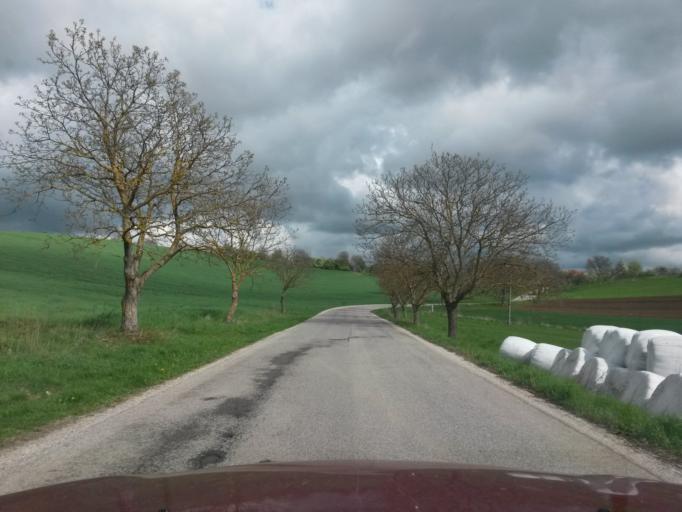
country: SK
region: Kosicky
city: Roznava
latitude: 48.5561
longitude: 20.5132
